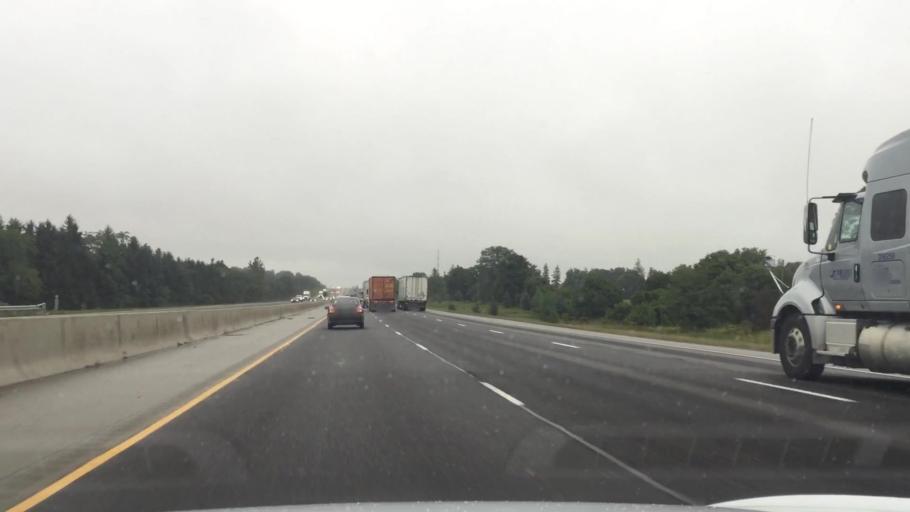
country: CA
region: Ontario
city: Kitchener
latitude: 43.2806
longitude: -80.5196
